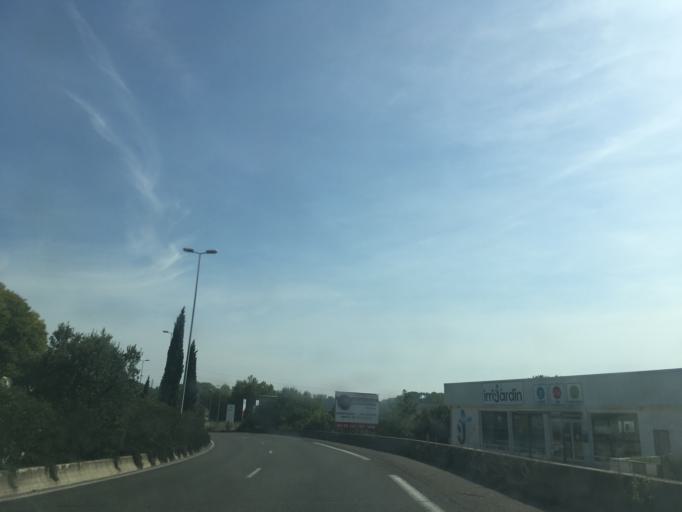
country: FR
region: Provence-Alpes-Cote d'Azur
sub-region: Departement du Var
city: Draguignan
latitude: 43.5176
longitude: 6.4732
